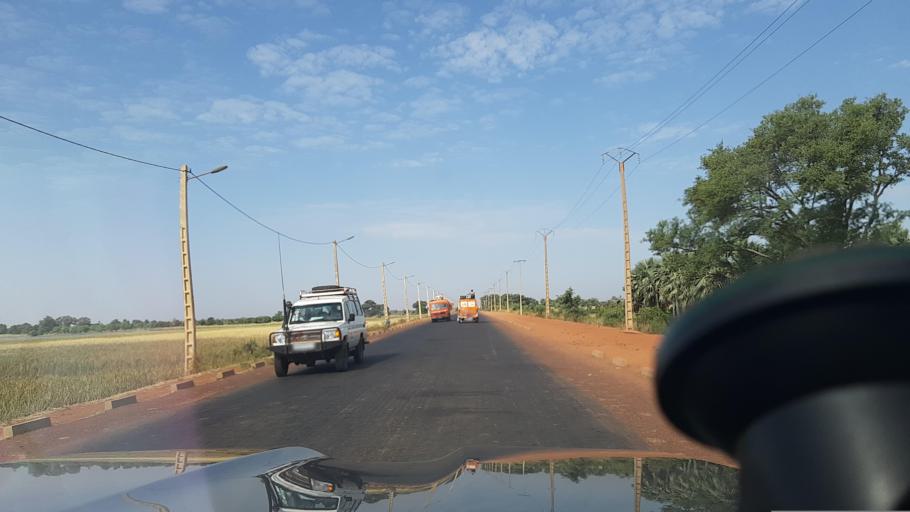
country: ML
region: Segou
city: Markala
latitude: 13.6842
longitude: -6.0928
